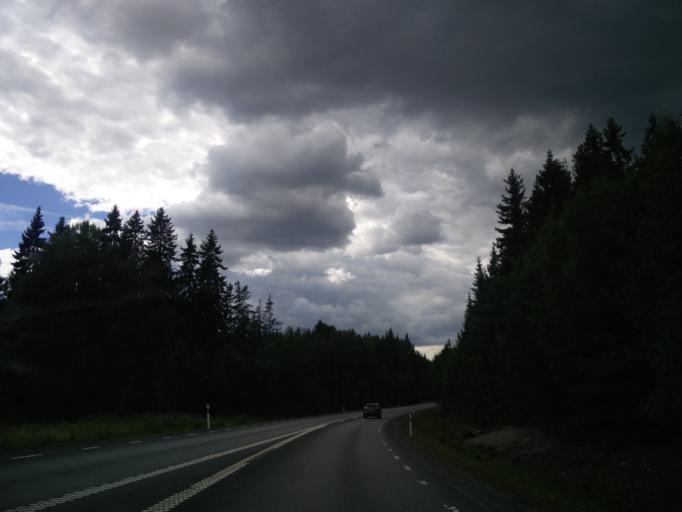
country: SE
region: OErebro
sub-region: Hallefors Kommun
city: Haellefors
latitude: 59.7981
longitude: 14.5734
